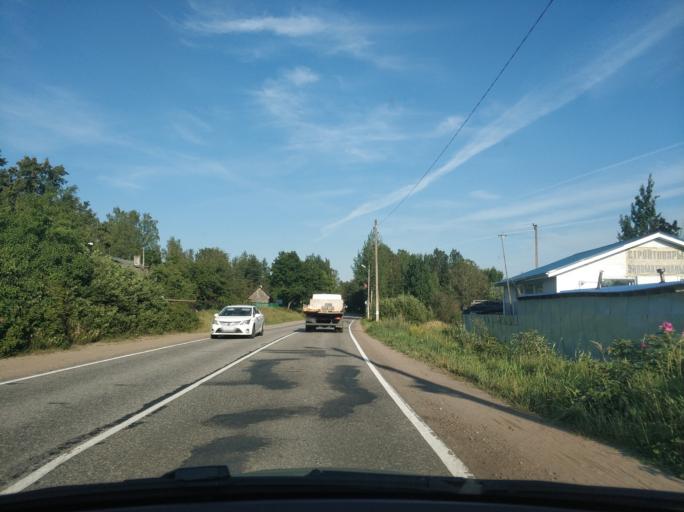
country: RU
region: Leningrad
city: Borisova Griva
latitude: 60.0935
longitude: 30.9806
